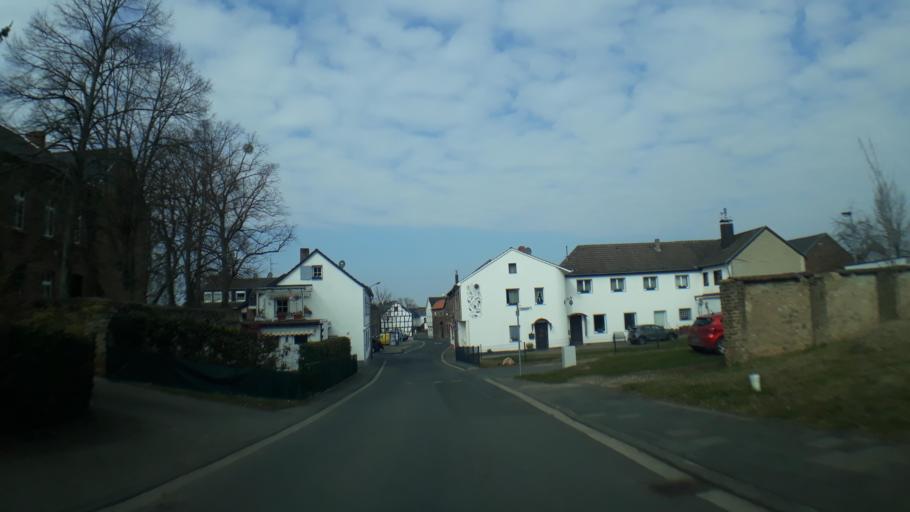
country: DE
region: North Rhine-Westphalia
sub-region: Regierungsbezirk Koln
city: Euskirchen
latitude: 50.6071
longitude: 6.8225
